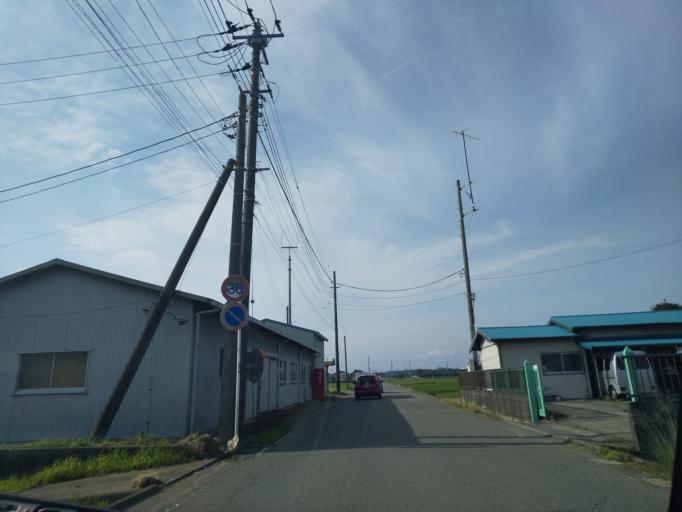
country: JP
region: Kanagawa
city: Zama
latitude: 35.4807
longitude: 139.3815
